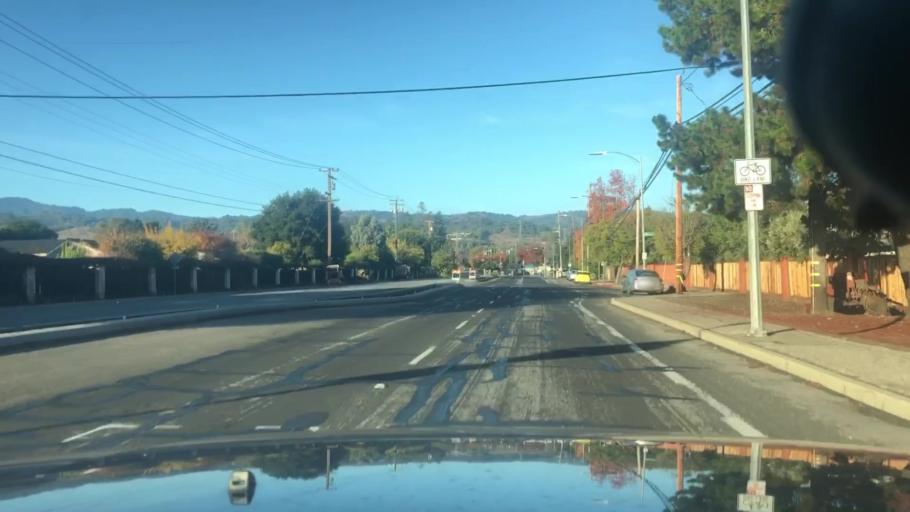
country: US
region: California
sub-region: Santa Clara County
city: Cupertino
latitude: 37.2940
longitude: -122.0283
